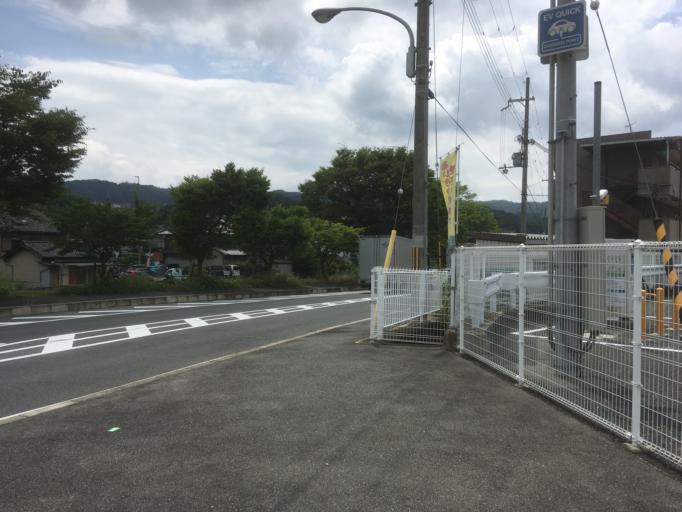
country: JP
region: Nara
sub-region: Ikoma-shi
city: Ikoma
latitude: 34.6659
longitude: 135.7074
